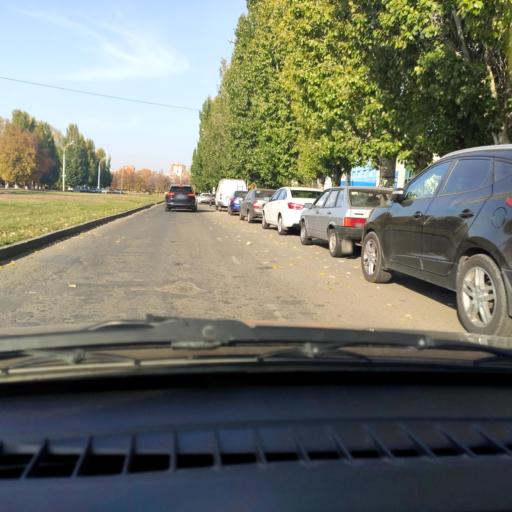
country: RU
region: Samara
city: Tol'yatti
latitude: 53.5162
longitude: 49.2857
